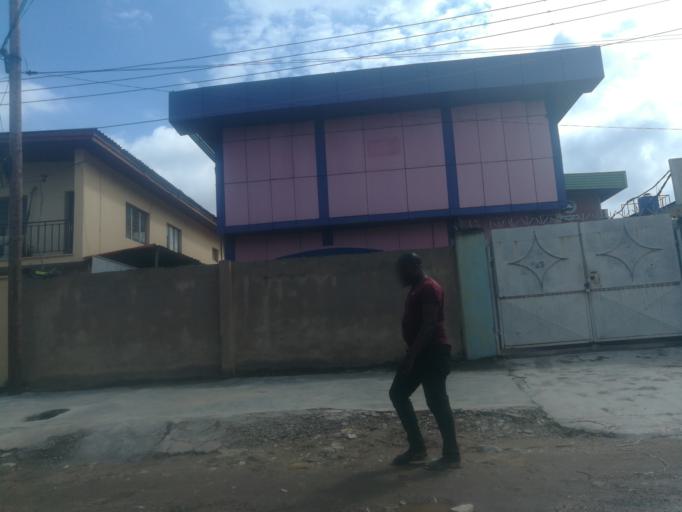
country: NG
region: Lagos
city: Somolu
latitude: 6.5484
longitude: 3.3755
